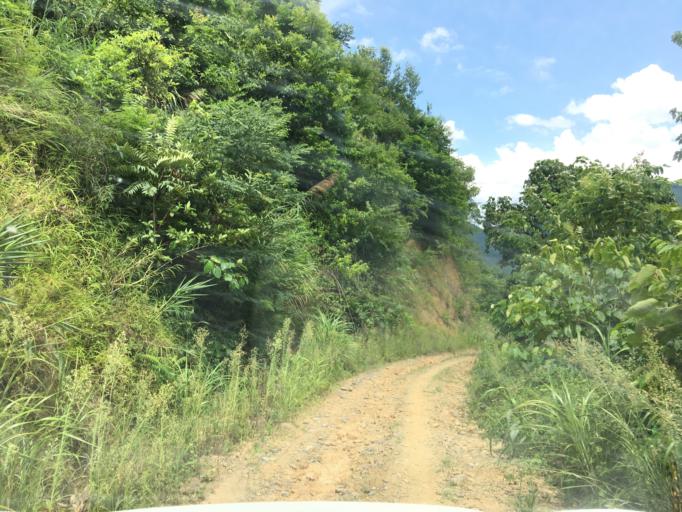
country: CN
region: Guangxi Zhuangzu Zizhiqu
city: Tongle
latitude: 24.9709
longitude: 105.9783
